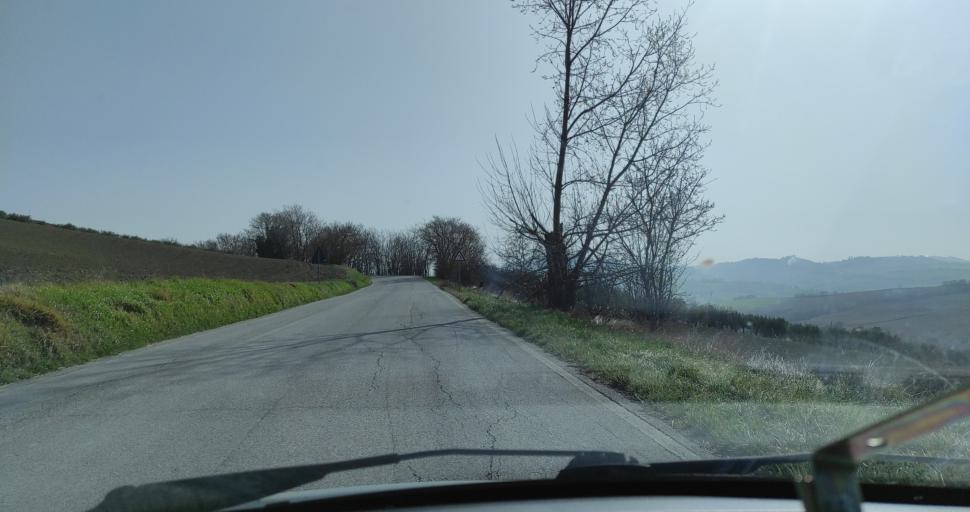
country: IT
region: The Marches
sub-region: Provincia di Macerata
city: Loro Piceno
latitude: 43.1787
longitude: 13.4438
